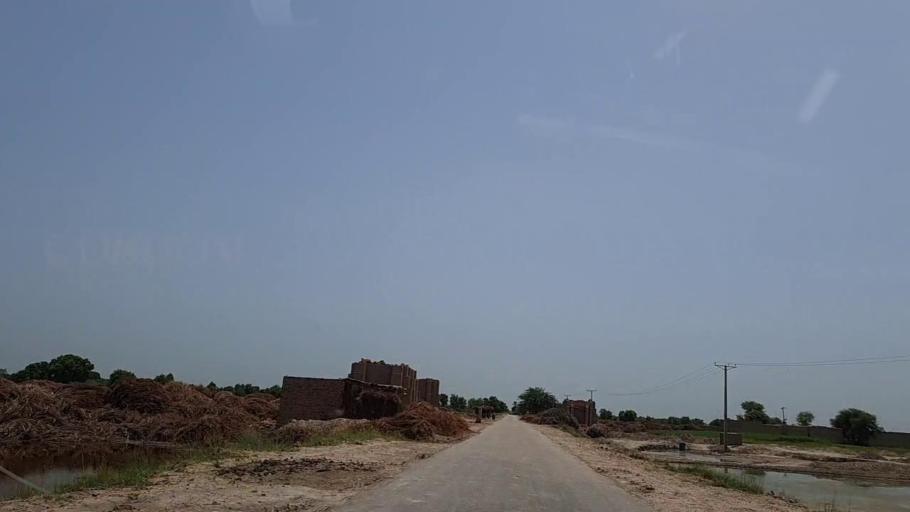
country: PK
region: Sindh
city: Tharu Shah
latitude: 26.9561
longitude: 68.0768
